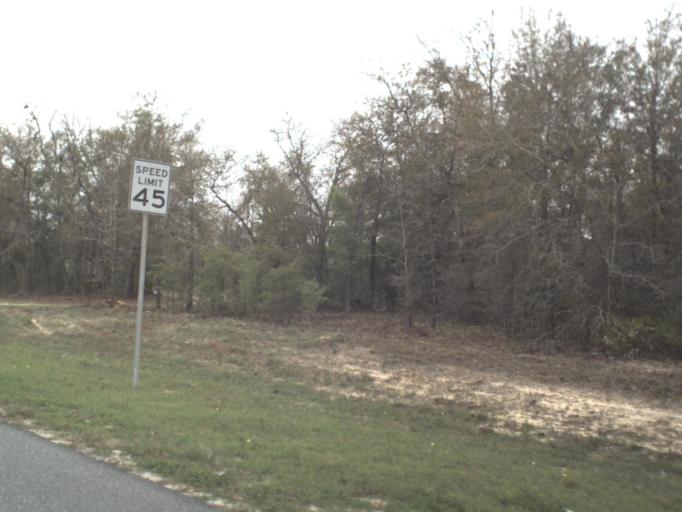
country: US
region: Florida
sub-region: Liberty County
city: Bristol
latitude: 30.4000
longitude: -84.7899
